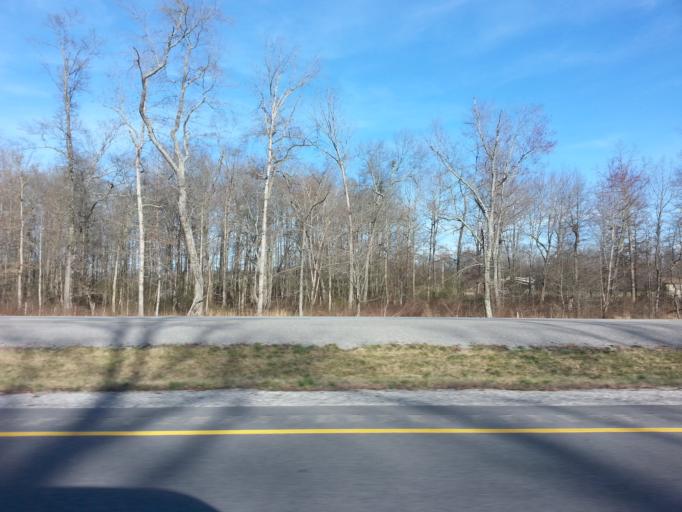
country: US
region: Tennessee
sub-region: Cannon County
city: Woodbury
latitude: 35.7584
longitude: -85.9665
